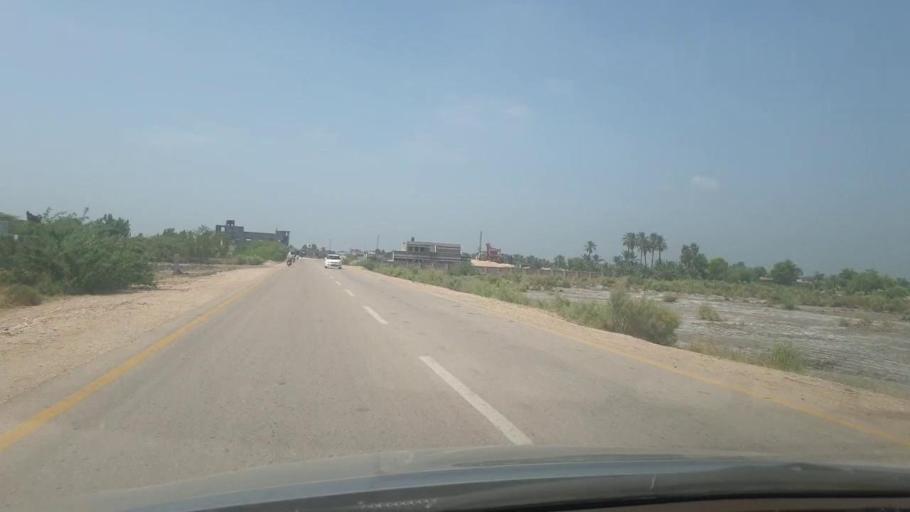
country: PK
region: Sindh
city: Bozdar
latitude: 27.2283
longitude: 68.5680
